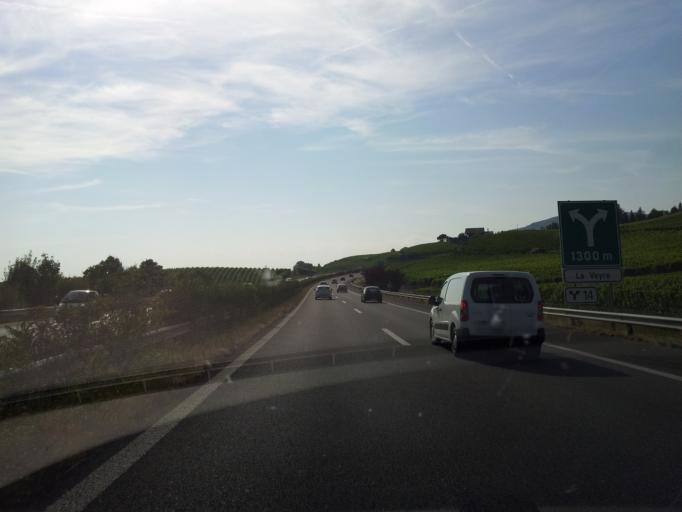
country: CH
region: Vaud
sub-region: Riviera-Pays-d'Enhaut District
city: Blonay
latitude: 46.4571
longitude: 6.8866
